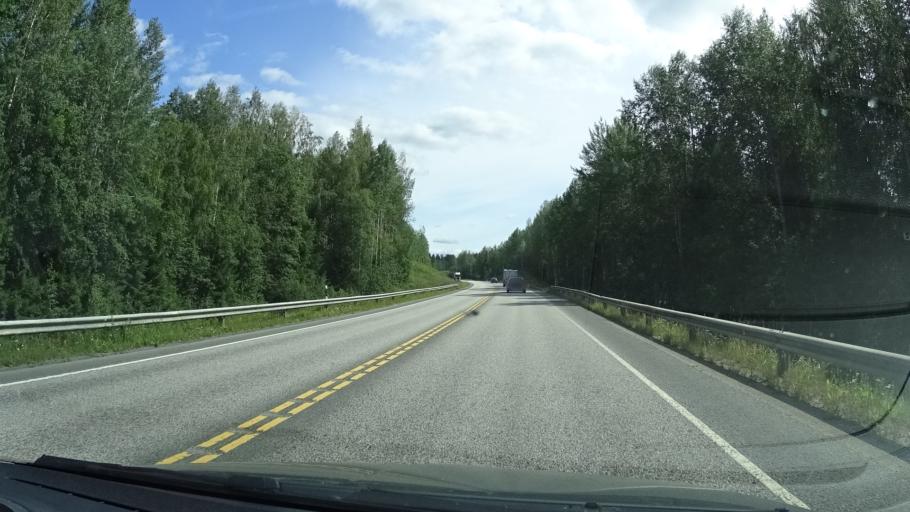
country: FI
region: Central Finland
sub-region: Jyvaeskylae
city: Jyvaeskylae
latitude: 62.2652
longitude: 25.5657
